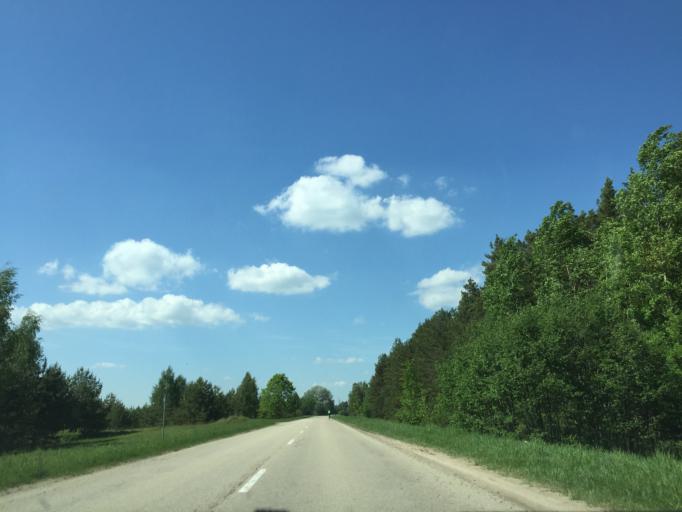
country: LV
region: Ozolnieku
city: Ozolnieki
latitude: 56.6143
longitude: 23.9385
